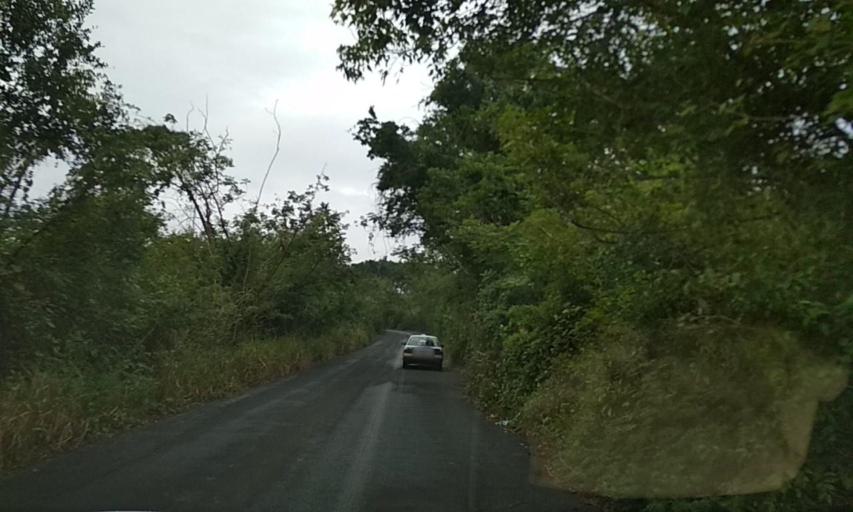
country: MX
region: Veracruz
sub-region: Coatzintla
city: Manuel Maria Contreras
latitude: 20.4476
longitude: -97.4981
